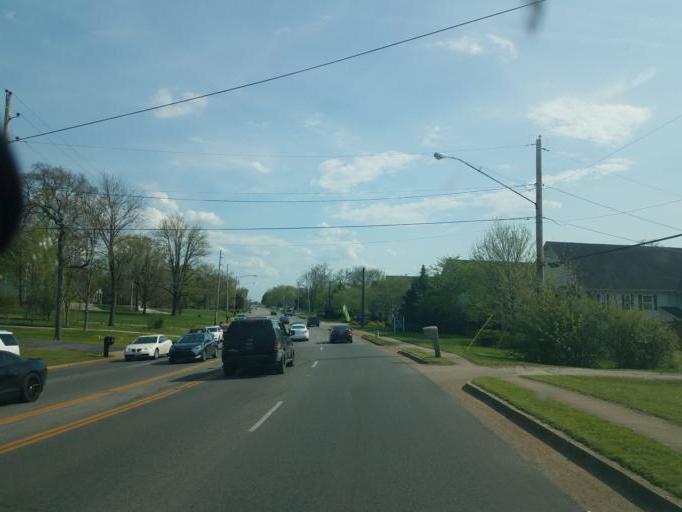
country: US
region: Kentucky
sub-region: Warren County
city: Bowling Green
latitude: 36.9785
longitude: -86.4382
